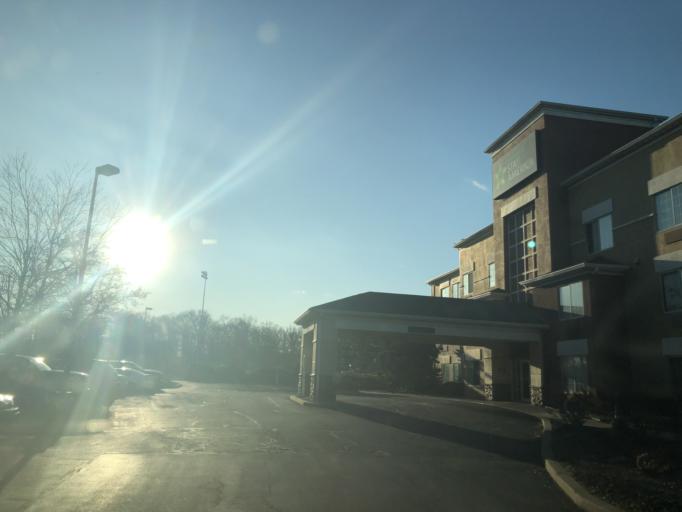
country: US
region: New Jersey
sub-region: Middlesex County
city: Fords
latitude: 40.5382
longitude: -74.2991
